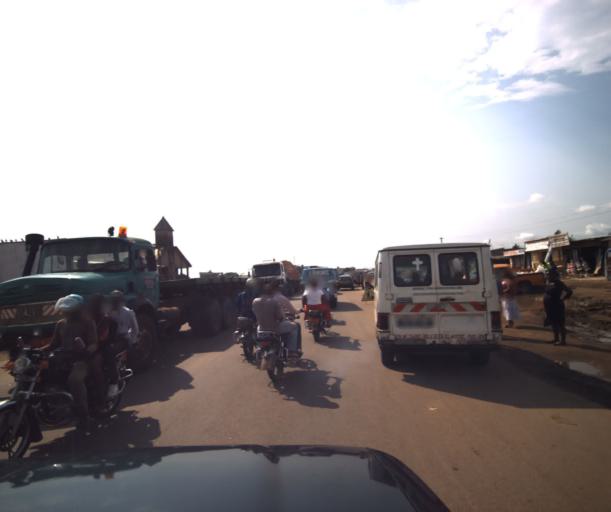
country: CM
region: Littoral
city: Douala
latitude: 4.0123
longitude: 9.7315
